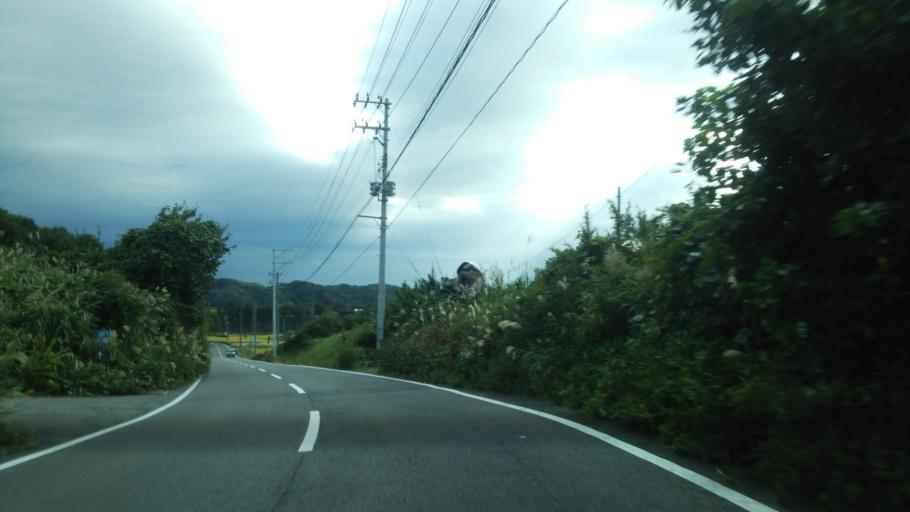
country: JP
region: Fukushima
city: Sukagawa
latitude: 37.2981
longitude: 140.2791
